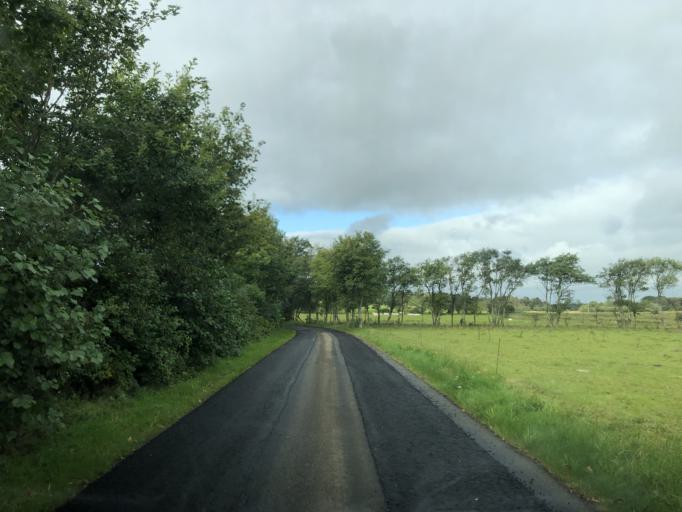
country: DK
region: Central Jutland
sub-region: Holstebro Kommune
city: Ulfborg
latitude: 56.2994
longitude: 8.4449
